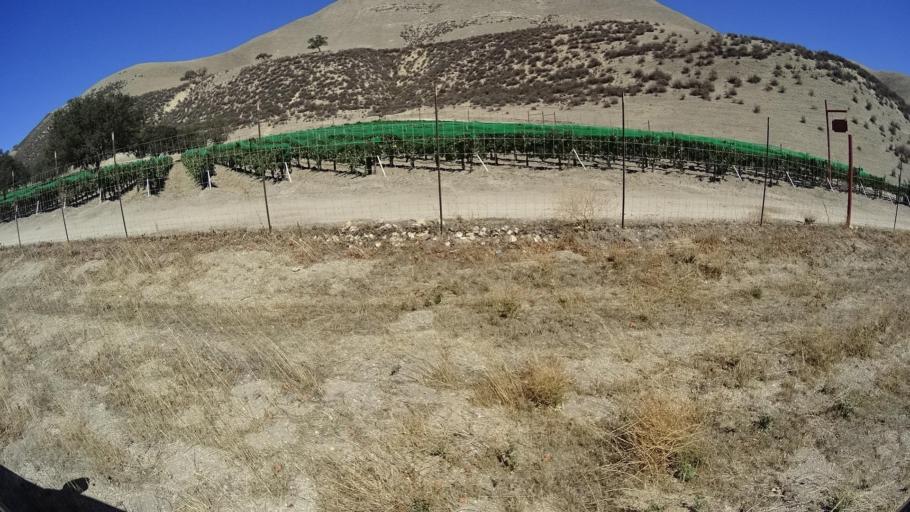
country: US
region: California
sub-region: Monterey County
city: Greenfield
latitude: 36.2718
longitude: -121.3996
